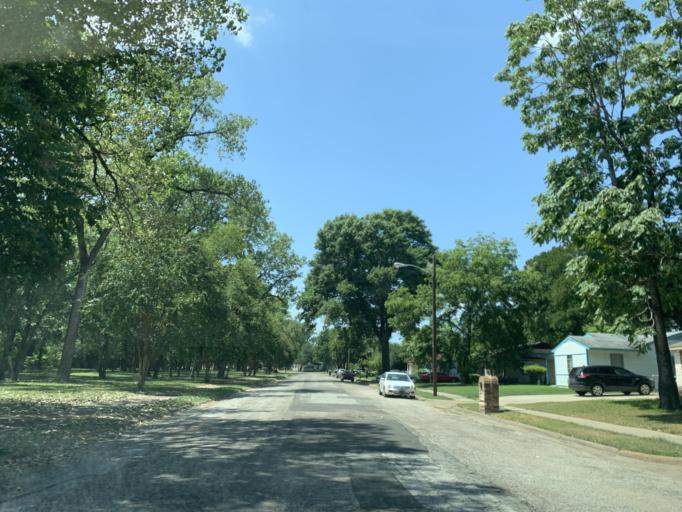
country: US
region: Texas
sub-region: Dallas County
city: Hutchins
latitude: 32.6843
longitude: -96.7752
